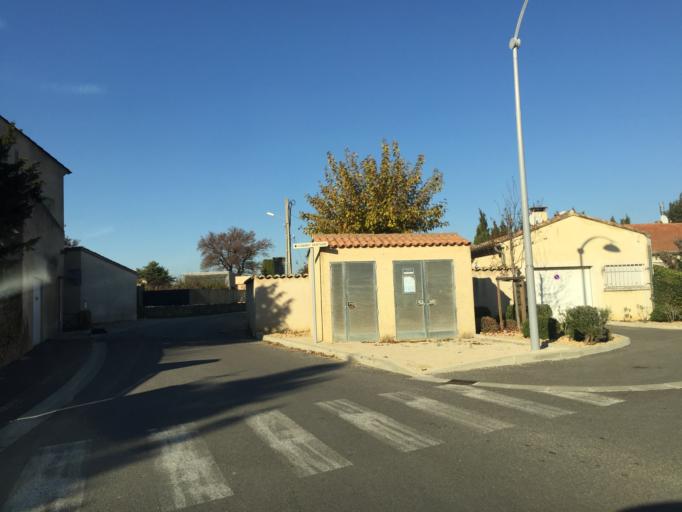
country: FR
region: Provence-Alpes-Cote d'Azur
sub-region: Departement du Vaucluse
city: Camaret-sur-Aigues
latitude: 44.1650
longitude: 4.8751
